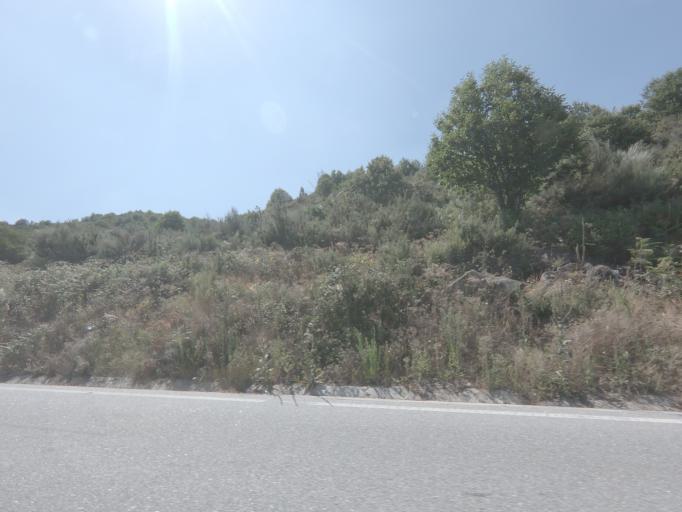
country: PT
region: Viseu
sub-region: Tarouca
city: Tarouca
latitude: 41.0117
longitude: -7.7842
